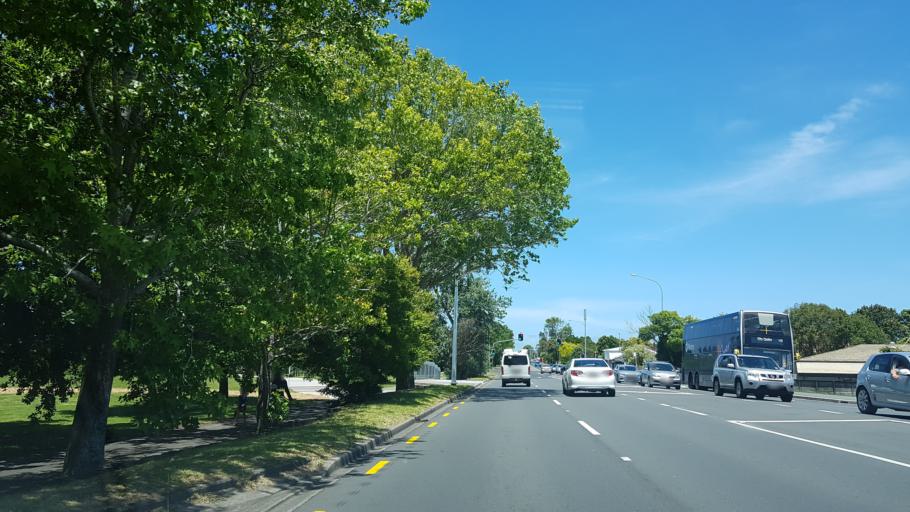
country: NZ
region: Auckland
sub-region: Auckland
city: Rosebank
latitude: -36.8784
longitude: 174.7027
